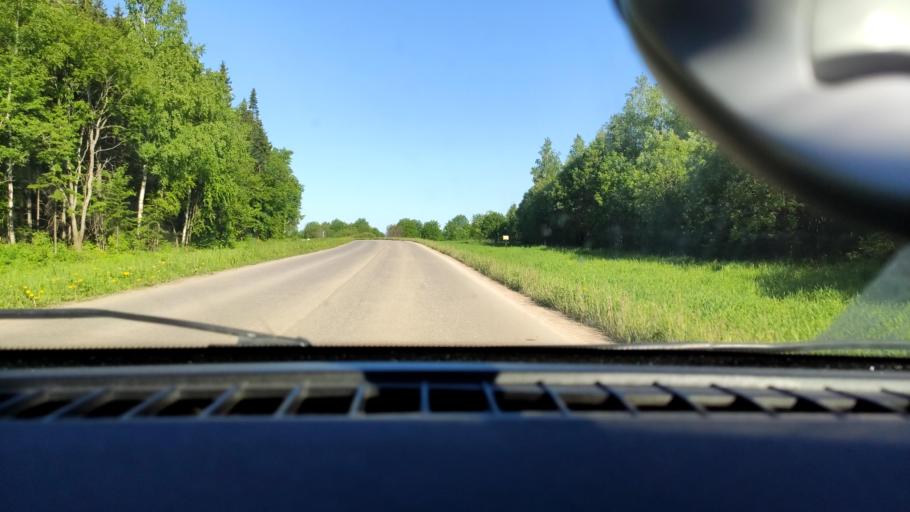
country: RU
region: Perm
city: Polazna
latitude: 58.2111
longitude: 56.4459
